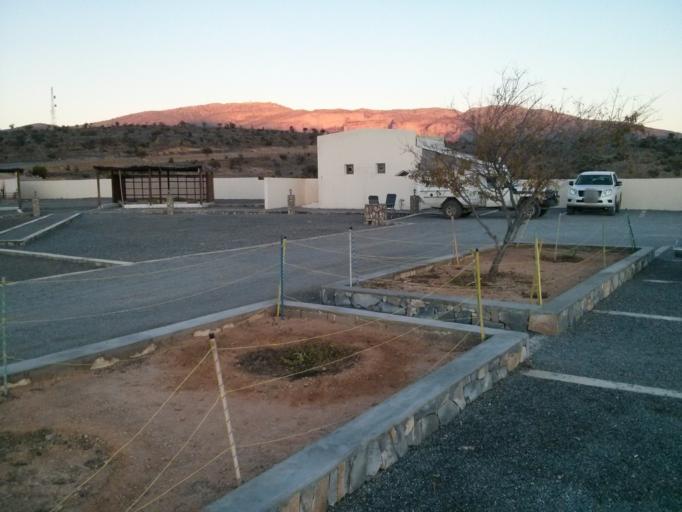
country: OM
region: Muhafazat ad Dakhiliyah
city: Bahla'
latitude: 23.2082
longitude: 57.1979
